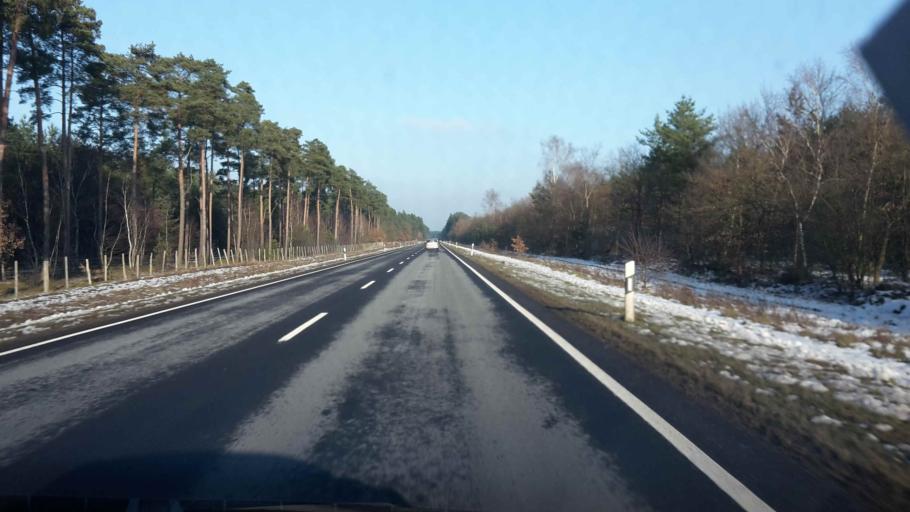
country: DE
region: Brandenburg
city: Weisen
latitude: 53.0416
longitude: 11.8122
